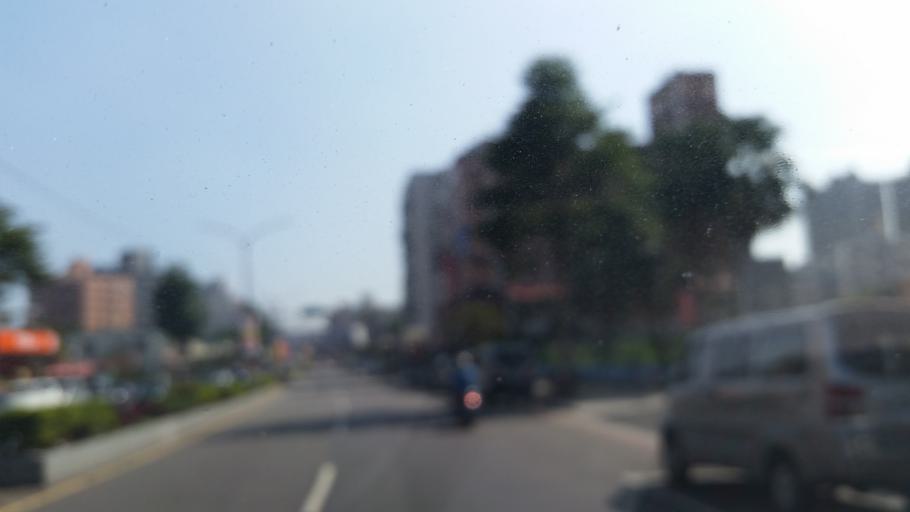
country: TW
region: Taipei
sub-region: Taipei
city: Banqiao
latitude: 25.0794
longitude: 121.3859
